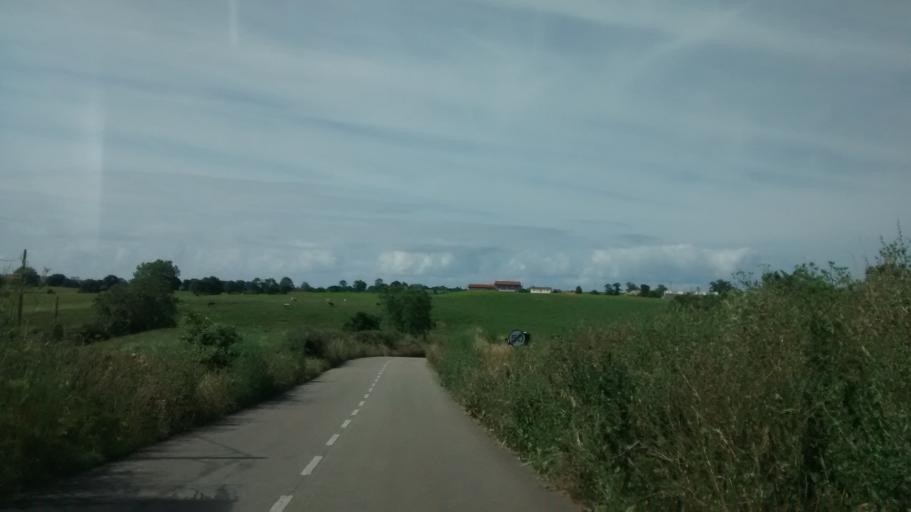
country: ES
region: Cantabria
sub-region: Provincia de Cantabria
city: Lierganes
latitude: 43.4133
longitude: -3.7437
